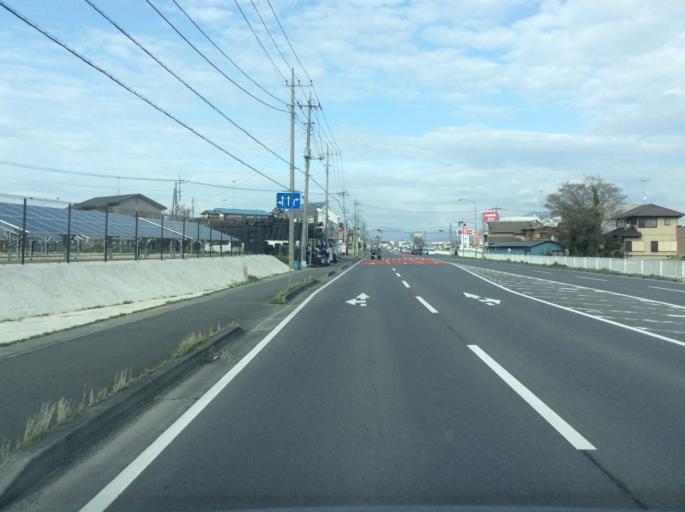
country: JP
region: Ibaraki
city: Ishige
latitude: 36.1820
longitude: 139.9746
